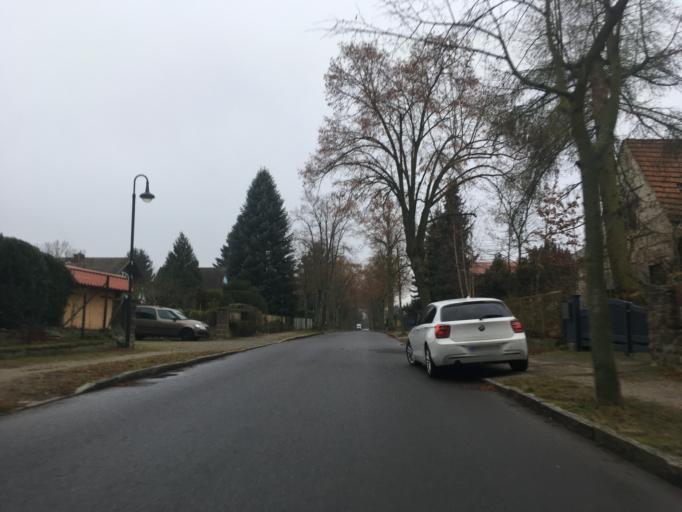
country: DE
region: Berlin
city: Buch
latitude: 52.6344
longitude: 13.5208
